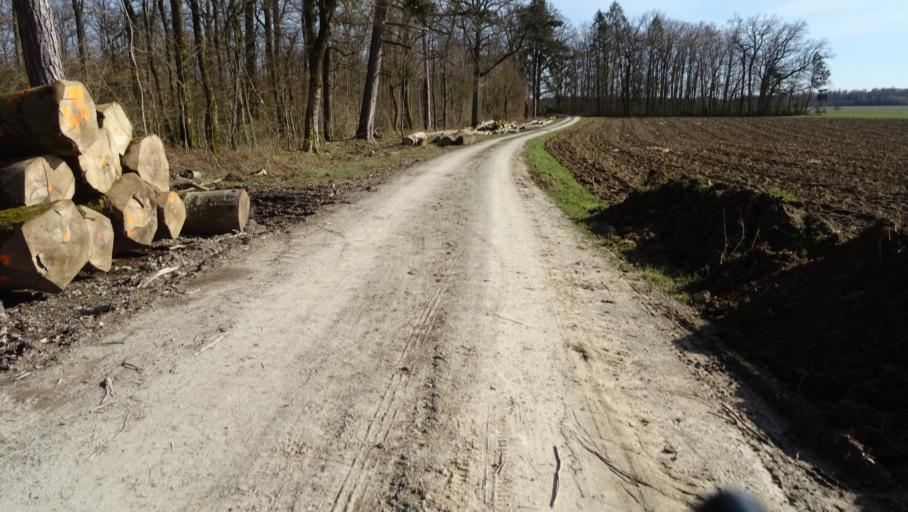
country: DE
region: Baden-Wuerttemberg
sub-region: Karlsruhe Region
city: Seckach
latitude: 49.4153
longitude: 9.3070
